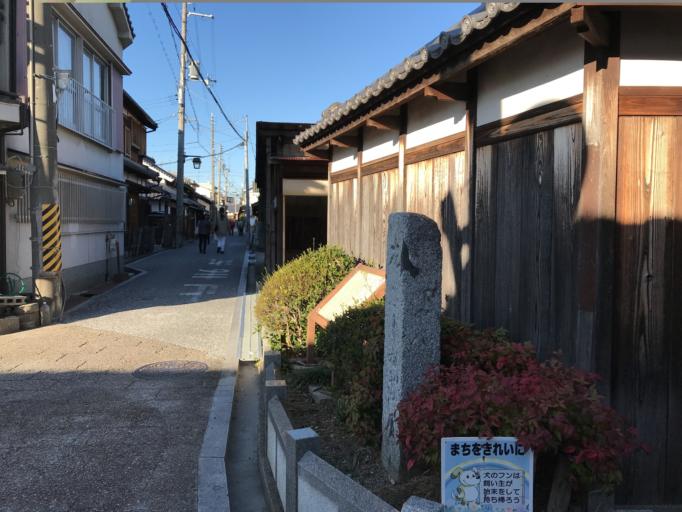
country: JP
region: Osaka
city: Tondabayashicho
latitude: 34.4989
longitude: 135.6019
